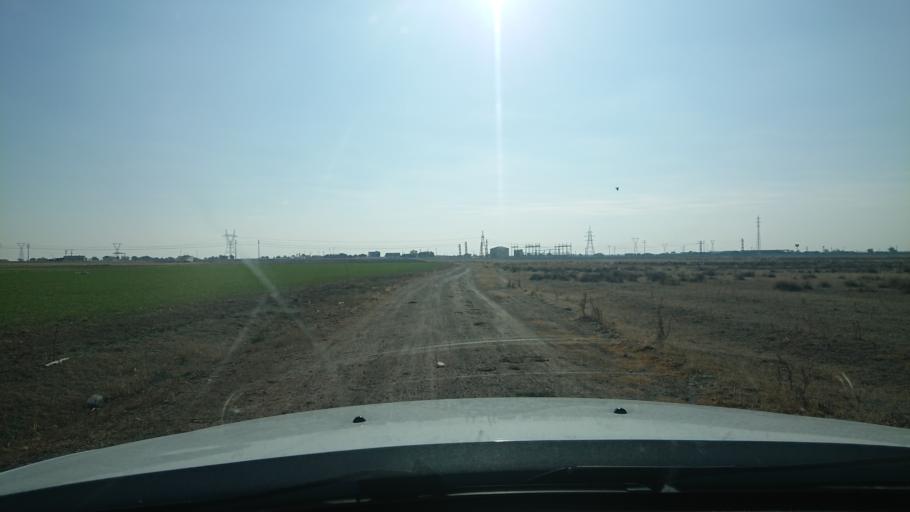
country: TR
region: Aksaray
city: Sultanhani
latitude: 38.2583
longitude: 33.4718
